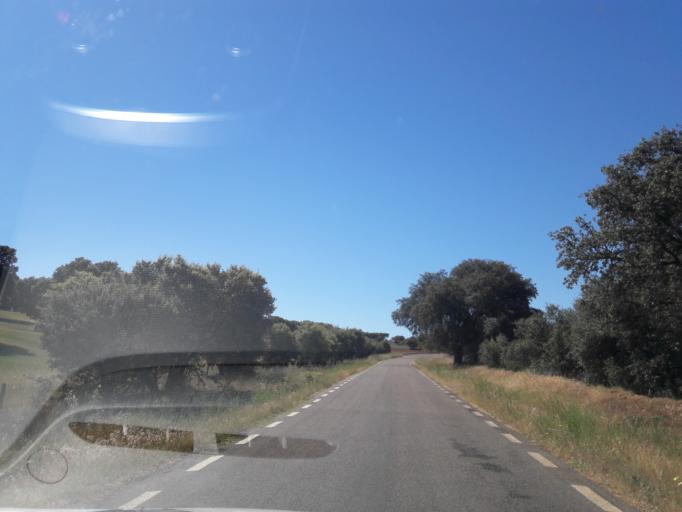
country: ES
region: Castille and Leon
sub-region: Provincia de Salamanca
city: Parada de Arriba
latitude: 41.0042
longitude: -5.8129
